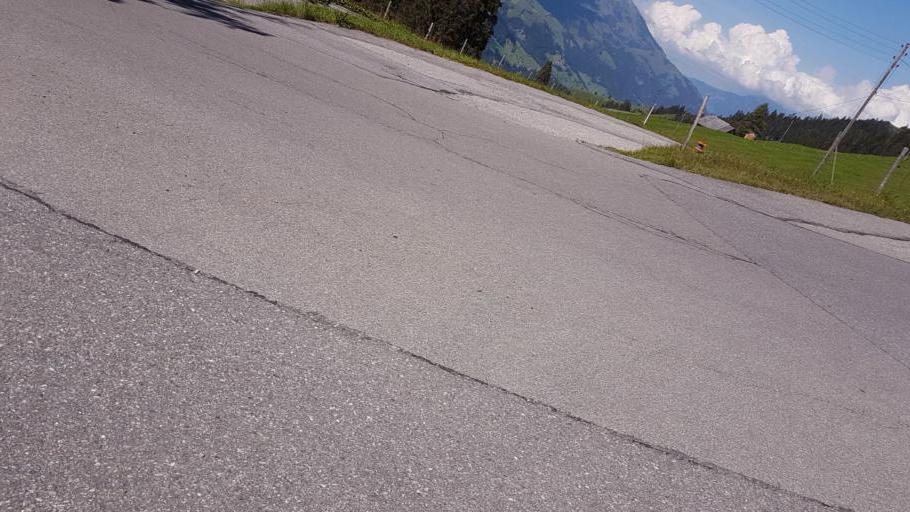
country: CH
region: Bern
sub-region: Frutigen-Niedersimmental District
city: Adelboden
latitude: 46.5171
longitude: 7.6033
